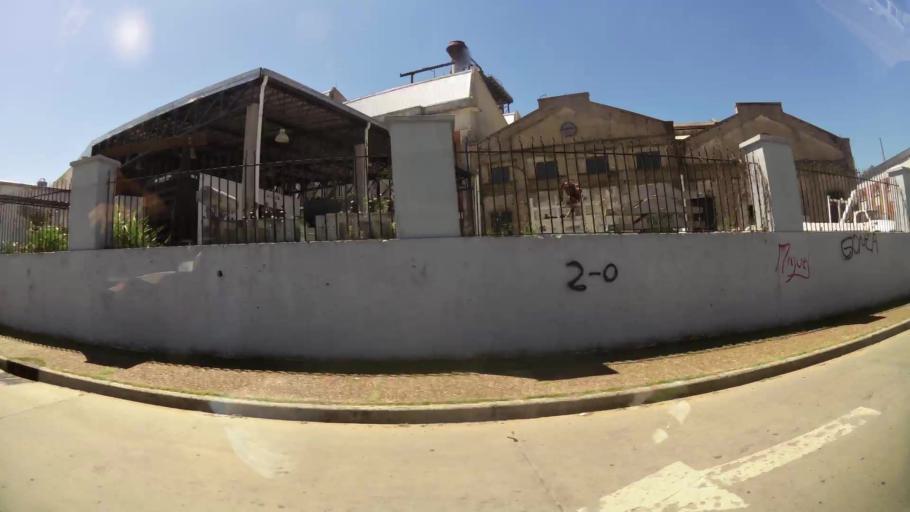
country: AR
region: Santa Fe
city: Santa Fe de la Vera Cruz
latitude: -31.6445
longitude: -60.6901
